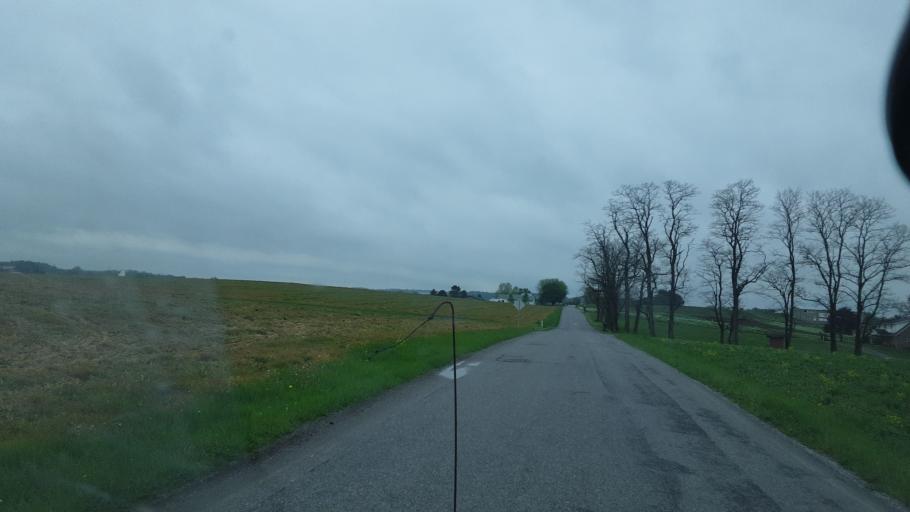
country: US
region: Ohio
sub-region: Holmes County
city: Millersburg
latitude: 40.5992
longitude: -81.8730
